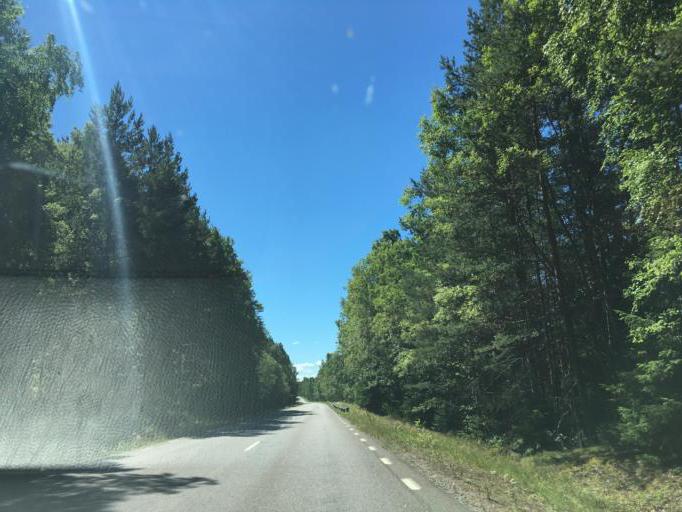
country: SE
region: OErebro
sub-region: Laxa Kommun
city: Laxa
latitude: 58.8427
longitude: 14.5480
